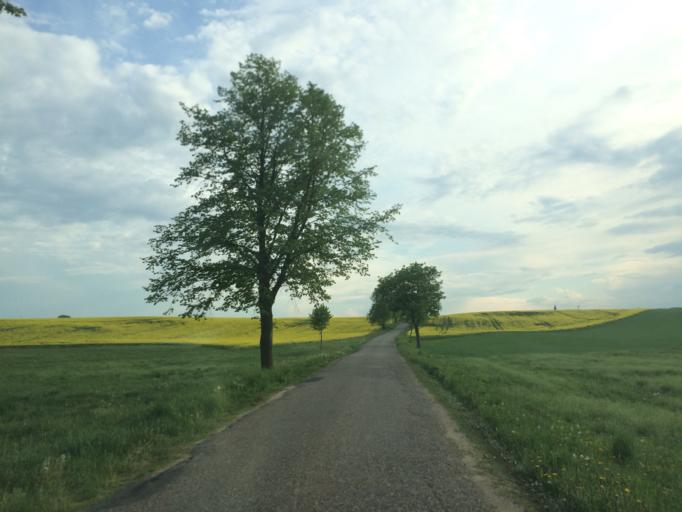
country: PL
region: Kujawsko-Pomorskie
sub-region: Powiat brodnicki
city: Brzozie
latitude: 53.3476
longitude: 19.5818
